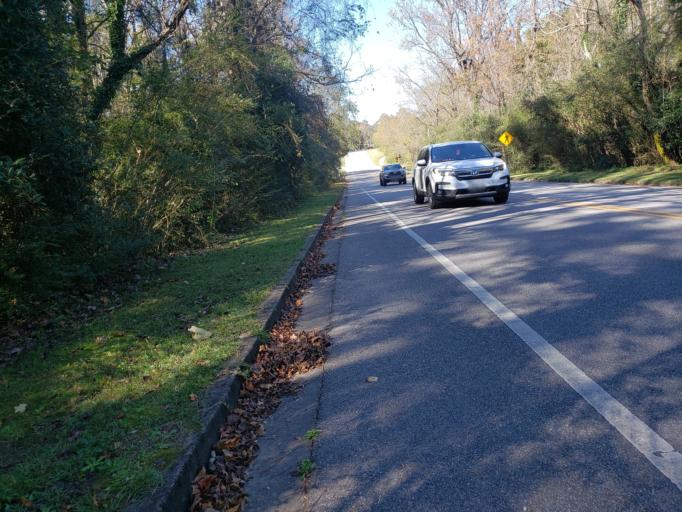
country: US
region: Alabama
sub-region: Lee County
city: Auburn
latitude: 32.5838
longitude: -85.4734
